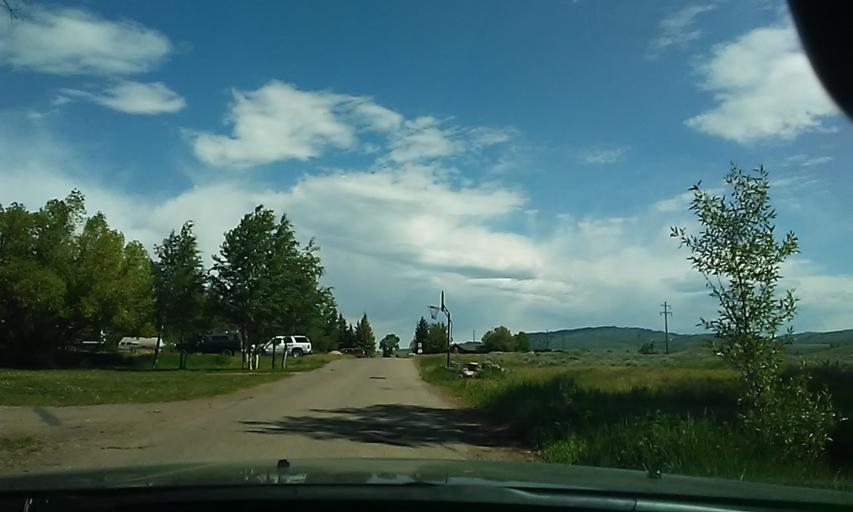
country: US
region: Wyoming
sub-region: Teton County
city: Jackson
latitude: 43.6229
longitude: -110.6239
